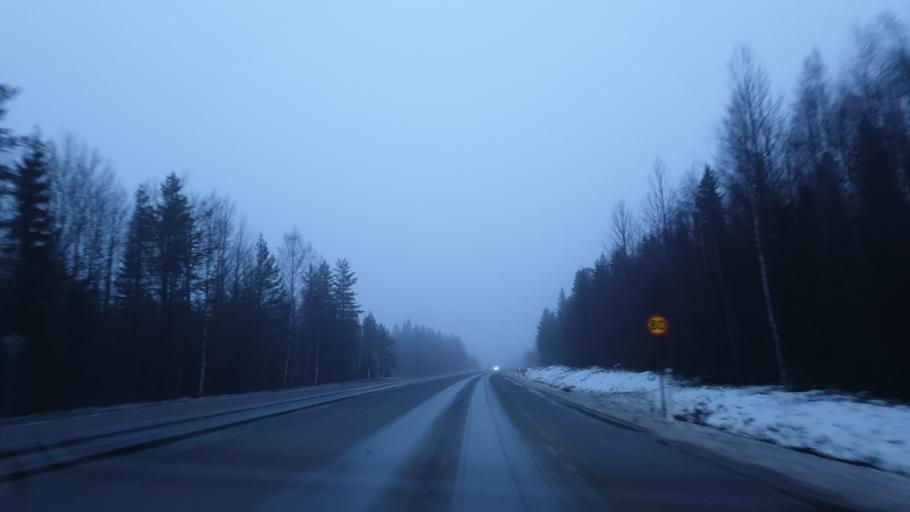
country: SE
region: Vaesterbotten
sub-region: Umea Kommun
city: Holmsund
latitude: 63.7641
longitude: 20.3410
